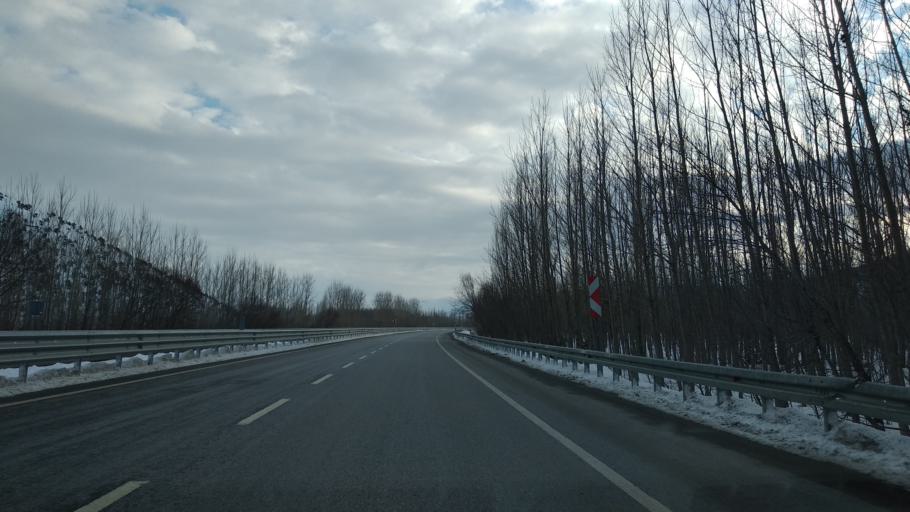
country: TR
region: Kahramanmaras
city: Goksun
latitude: 38.0526
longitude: 36.4691
